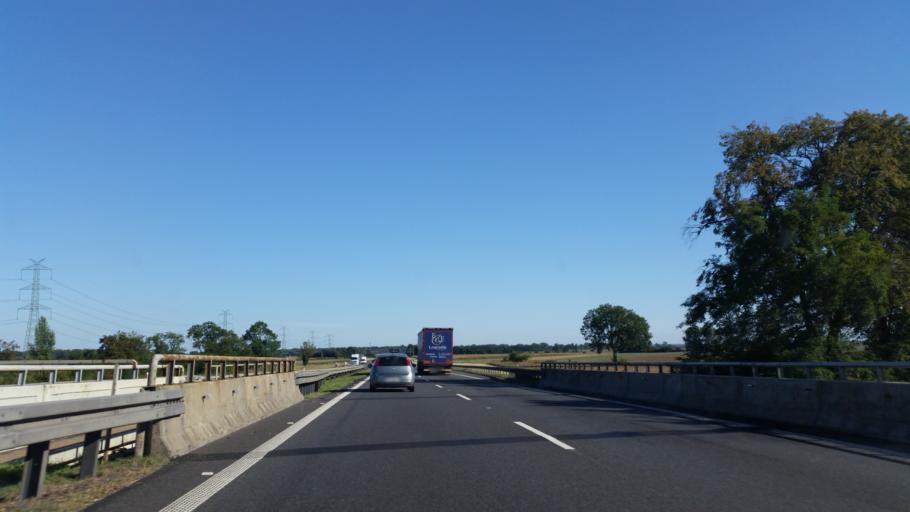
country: PL
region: Lower Silesian Voivodeship
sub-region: Powiat strzelinski
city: Wiazow
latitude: 50.8672
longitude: 17.2166
